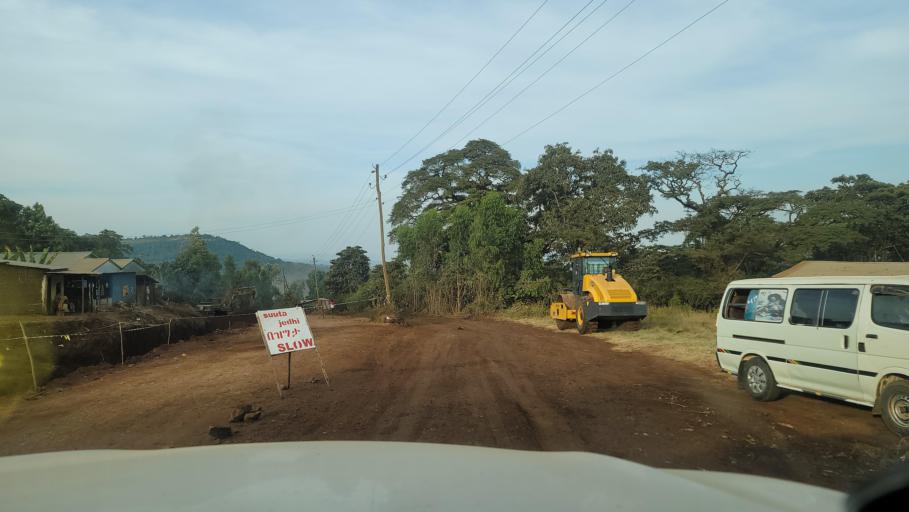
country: ET
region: Oromiya
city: Agaro
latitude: 7.8262
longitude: 36.5416
